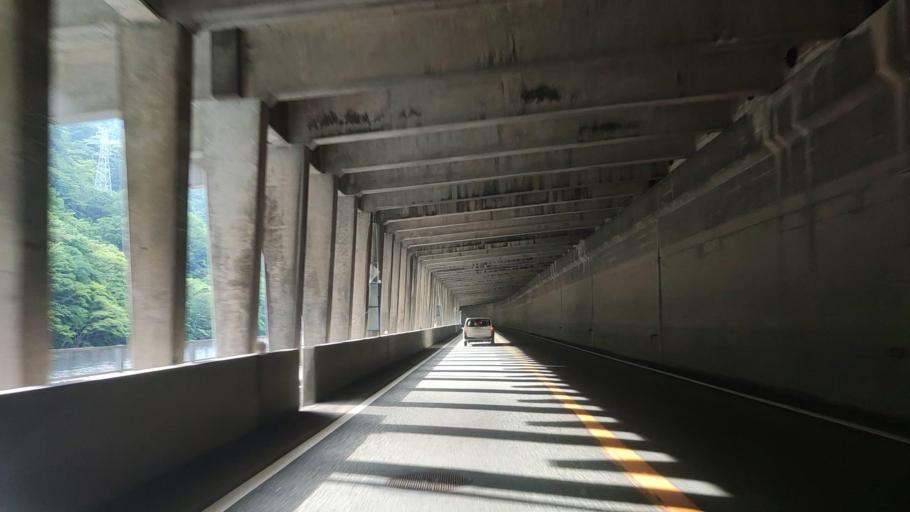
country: JP
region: Toyama
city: Yatsuomachi-higashikumisaka
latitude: 36.4156
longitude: 137.2900
